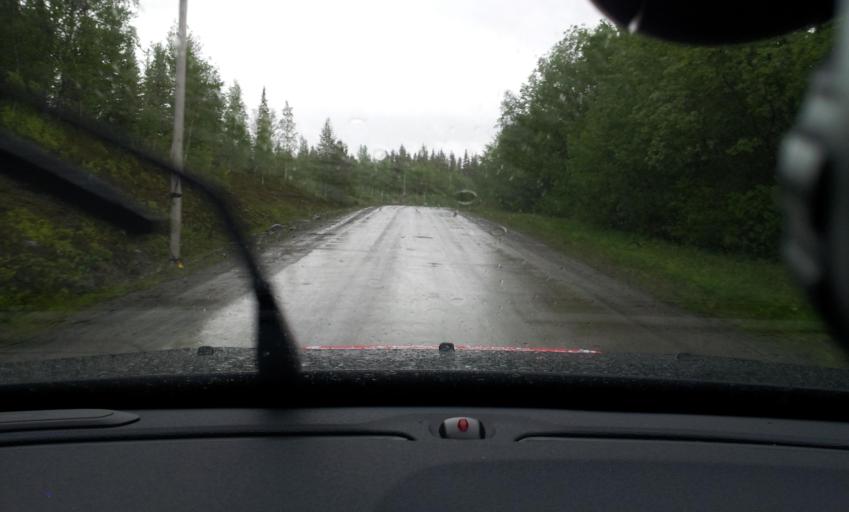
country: SE
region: Jaemtland
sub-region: Are Kommun
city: Are
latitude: 63.2185
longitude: 13.0656
